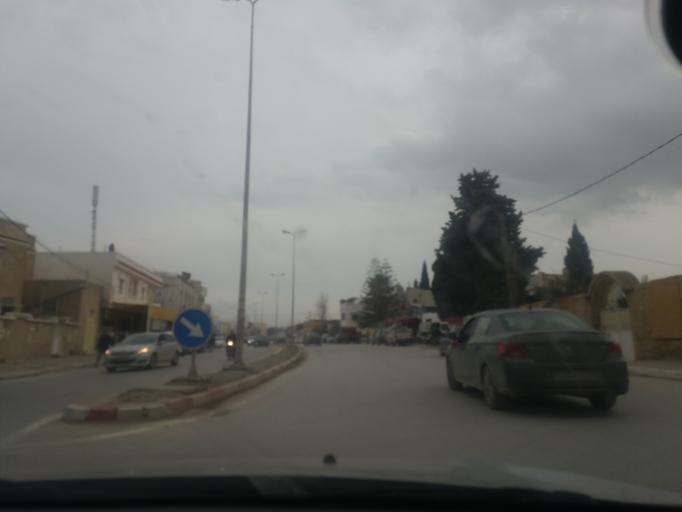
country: TN
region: Ariana
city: Ariana
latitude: 36.8726
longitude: 10.1815
